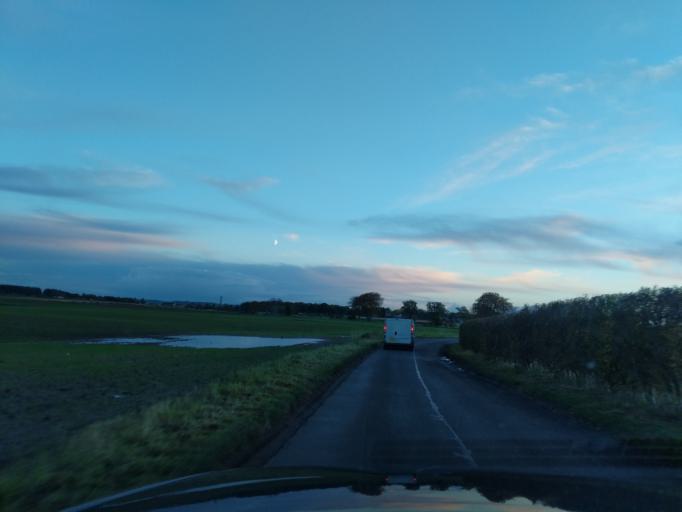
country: GB
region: Scotland
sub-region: Fife
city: Leuchars
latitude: 56.3907
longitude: -2.8749
